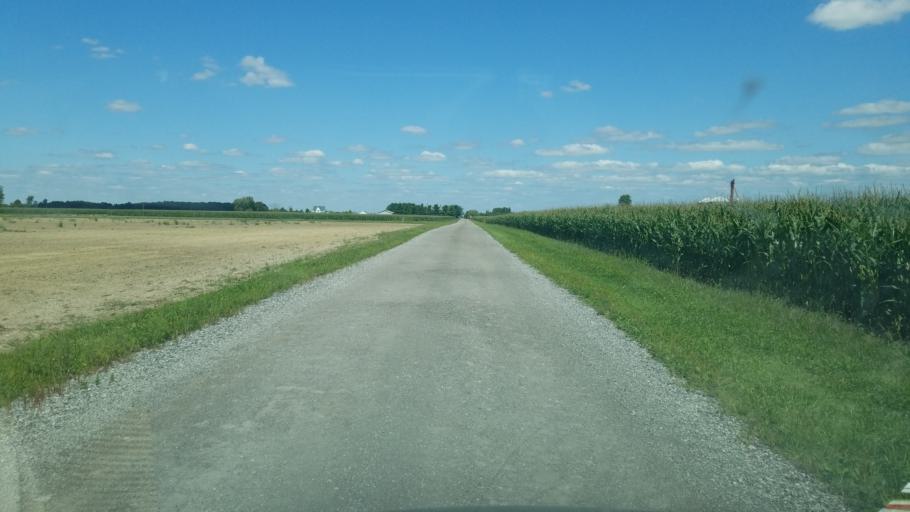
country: US
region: Ohio
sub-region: Fulton County
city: Delta
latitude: 41.6792
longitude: -84.0167
